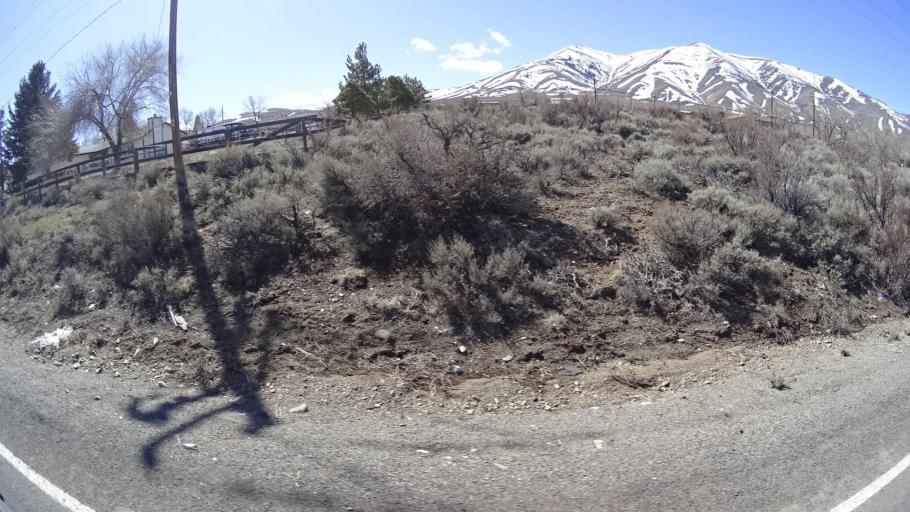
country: US
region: Nevada
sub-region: Washoe County
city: Lemmon Valley
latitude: 39.6232
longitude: -119.9042
